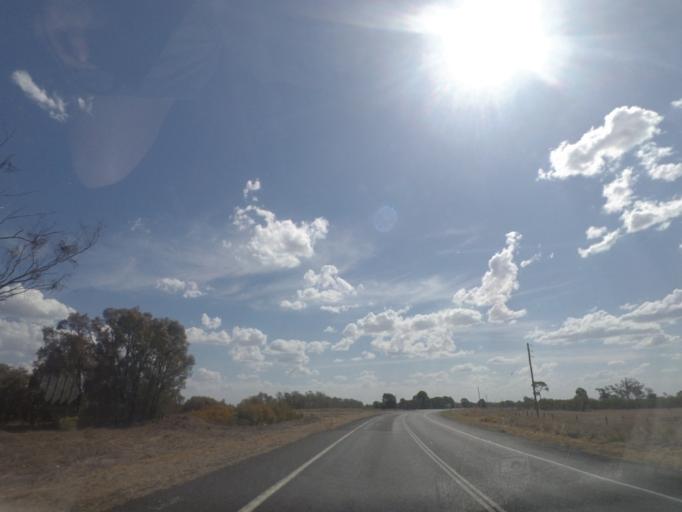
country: AU
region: Queensland
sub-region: Southern Downs
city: Stanthorpe
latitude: -28.4137
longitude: 151.1644
